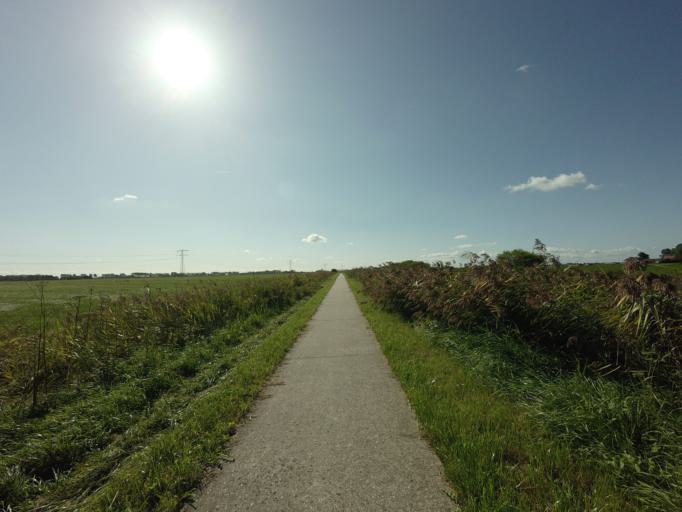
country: NL
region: Friesland
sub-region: Gemeente Boarnsterhim
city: Reduzum
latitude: 53.1467
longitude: 5.7639
